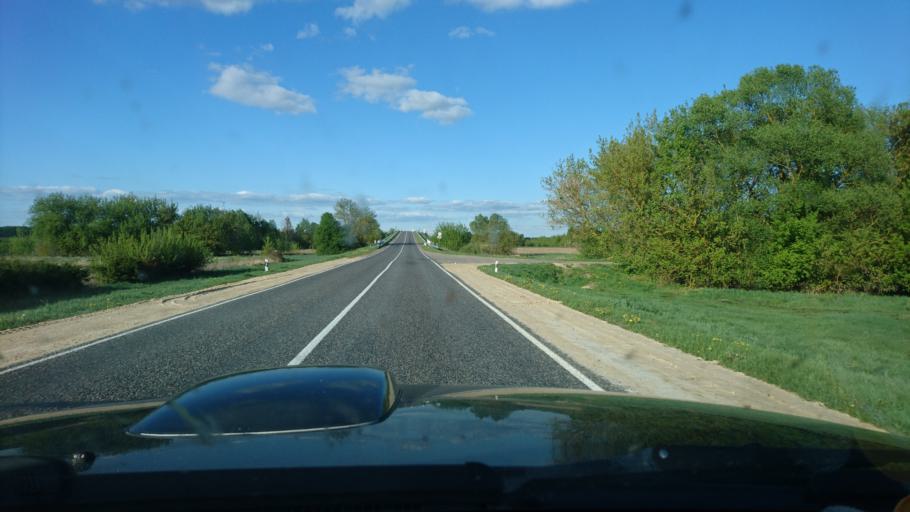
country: BY
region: Brest
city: Nyakhachava
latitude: 52.6364
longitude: 25.1902
